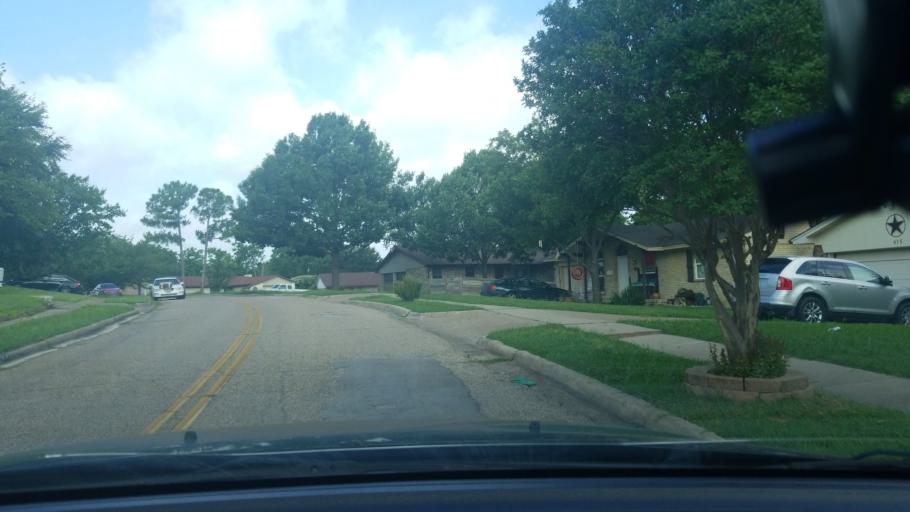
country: US
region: Texas
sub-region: Dallas County
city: Mesquite
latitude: 32.7736
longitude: -96.6344
